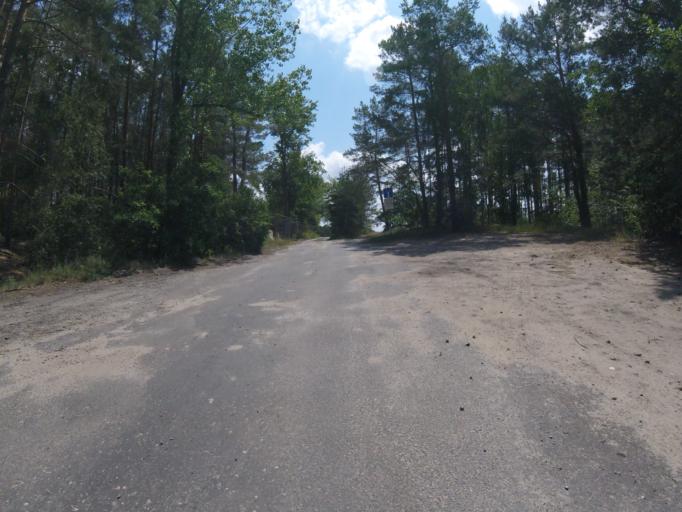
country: DE
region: Brandenburg
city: Bestensee
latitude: 52.2842
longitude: 13.6726
